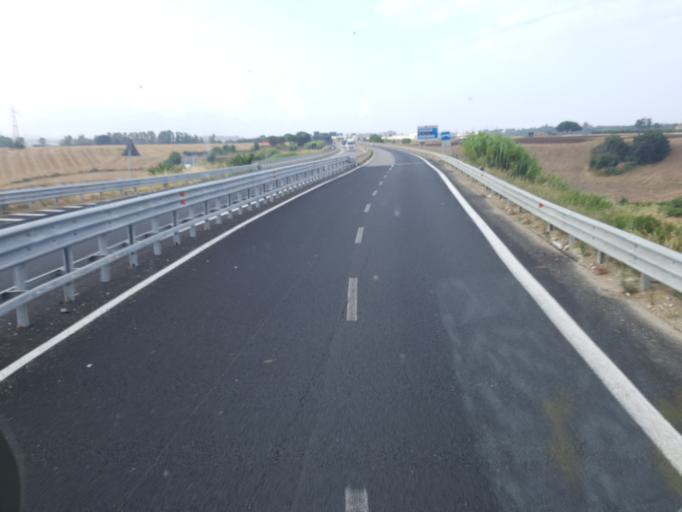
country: IT
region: Latium
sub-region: Citta metropolitana di Roma Capitale
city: Aurelia
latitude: 42.1615
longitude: 11.7884
